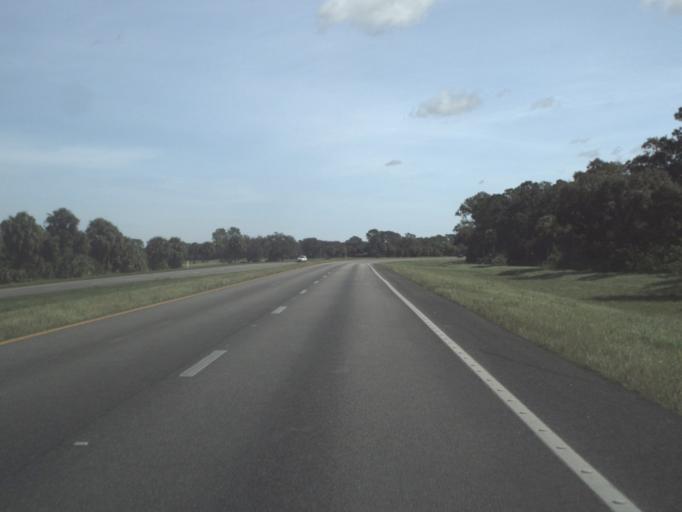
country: US
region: Florida
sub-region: Hendry County
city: Port LaBelle
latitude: 26.7660
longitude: -81.3809
